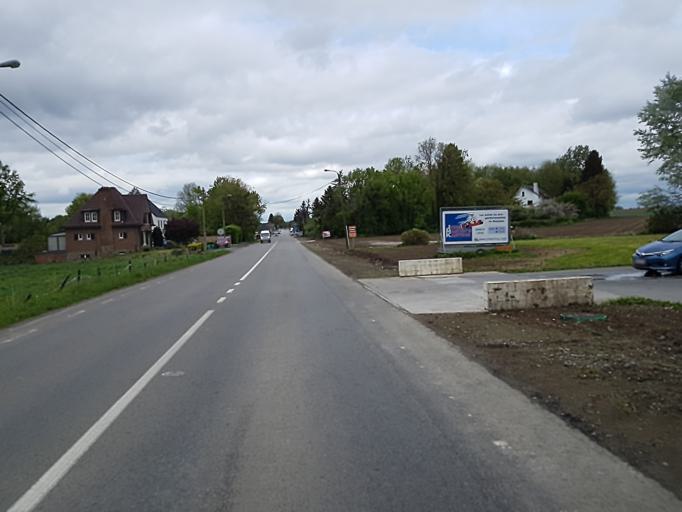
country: BE
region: Wallonia
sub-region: Province du Brabant Wallon
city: Jodoigne
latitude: 50.7398
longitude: 4.8804
